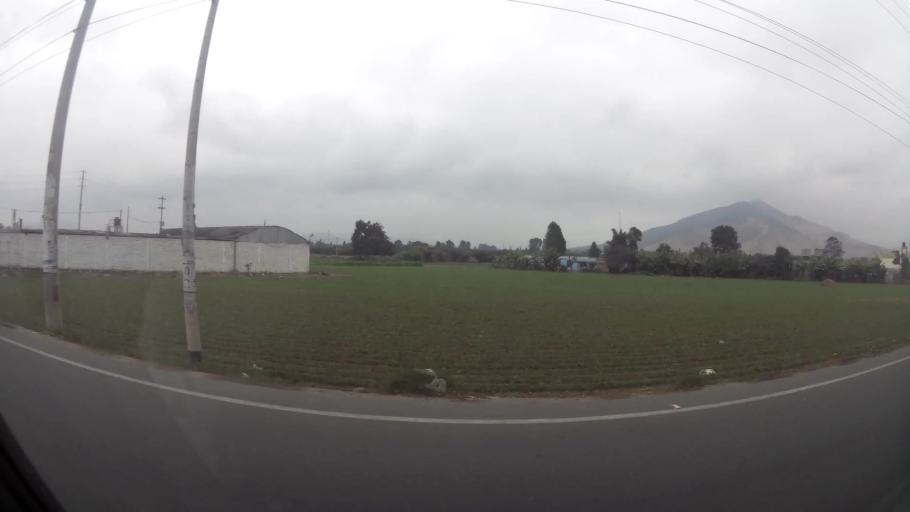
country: PE
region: Lima
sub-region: Provincia de Huaral
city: Huaral
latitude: -11.5108
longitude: -77.2327
